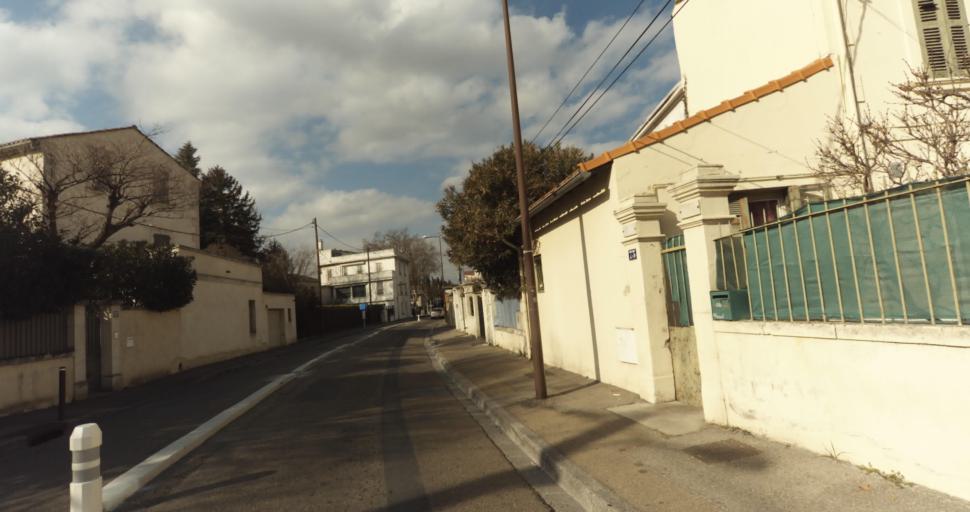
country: FR
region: Provence-Alpes-Cote d'Azur
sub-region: Departement du Vaucluse
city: Avignon
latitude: 43.9371
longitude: 4.8149
